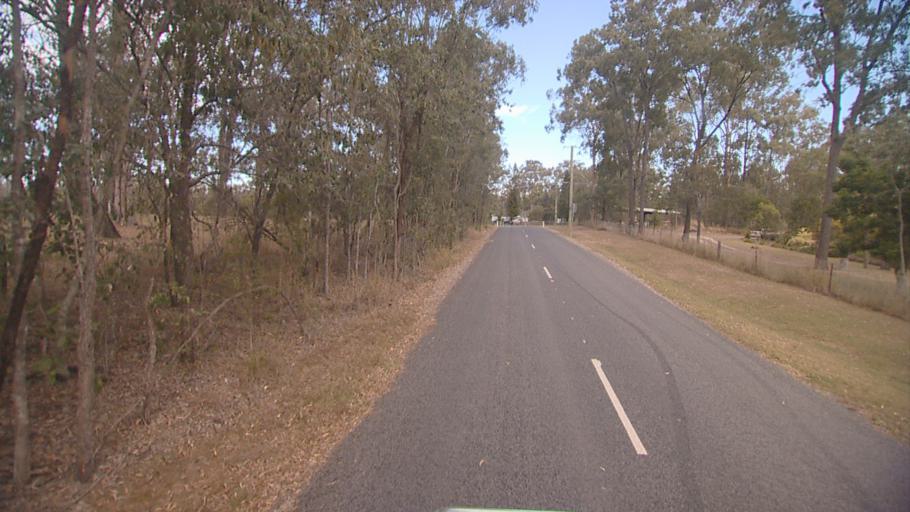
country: AU
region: Queensland
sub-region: Logan
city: North Maclean
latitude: -27.7641
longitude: 152.9702
